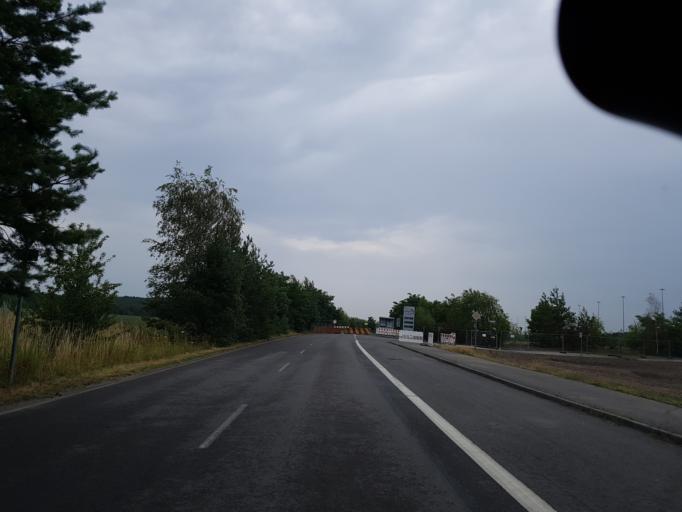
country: DE
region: Brandenburg
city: Schipkau
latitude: 51.5445
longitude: 13.9283
